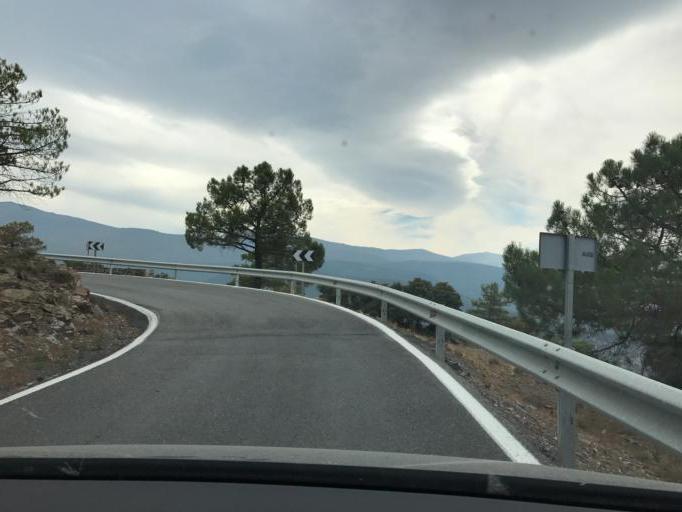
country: ES
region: Andalusia
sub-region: Provincia de Granada
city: Aldeire
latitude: 37.1595
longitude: -3.0571
